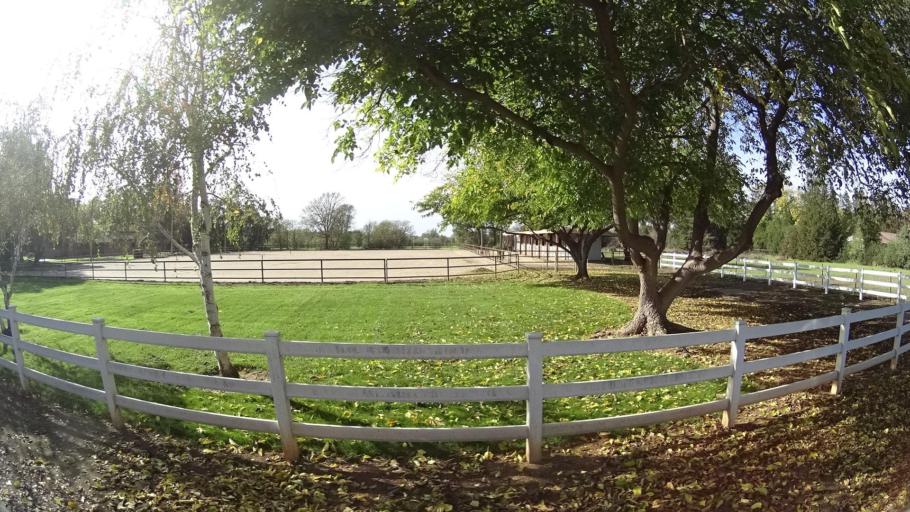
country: US
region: California
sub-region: Sacramento County
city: Vineyard
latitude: 38.4399
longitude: -121.3115
